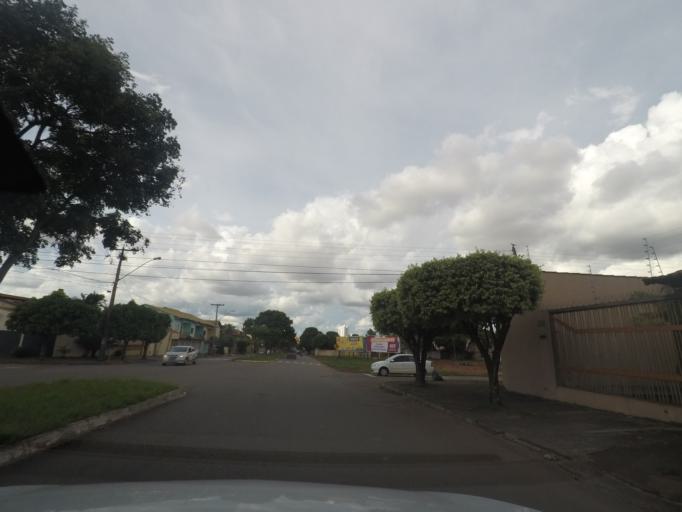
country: BR
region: Goias
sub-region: Goiania
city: Goiania
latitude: -16.7176
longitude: -49.3049
